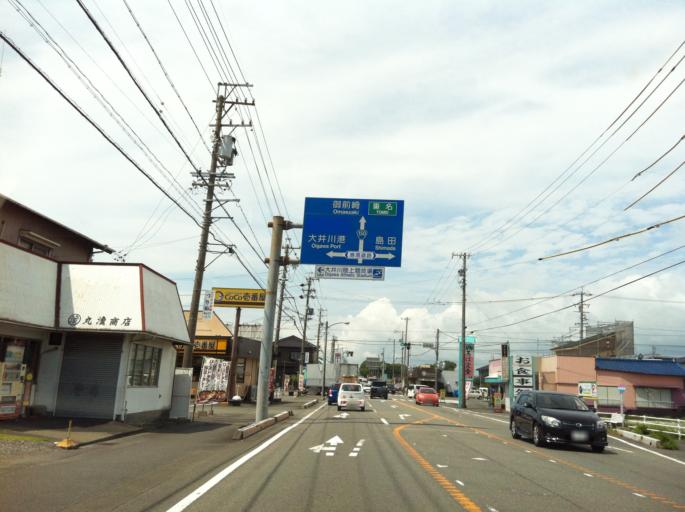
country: JP
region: Shizuoka
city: Fujieda
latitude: 34.8056
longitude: 138.2672
